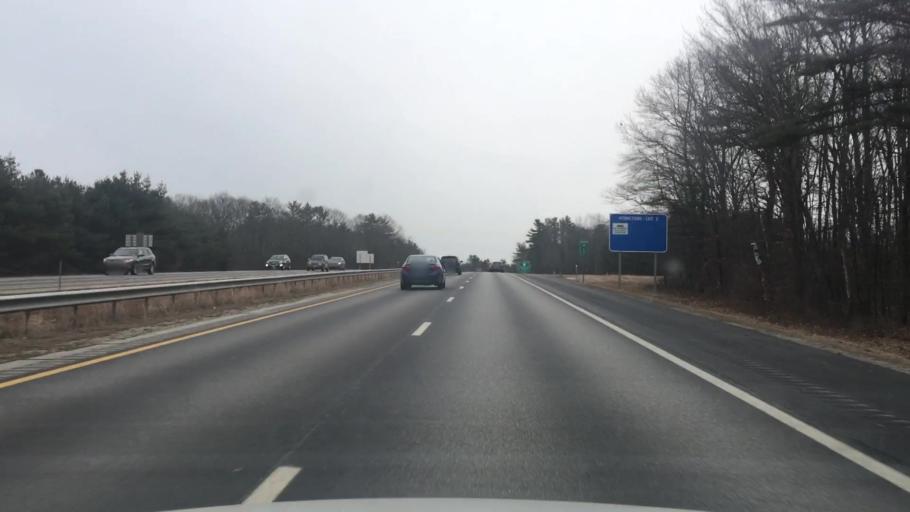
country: US
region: New Hampshire
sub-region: Merrimack County
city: Concord
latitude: 43.1837
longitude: -71.5803
